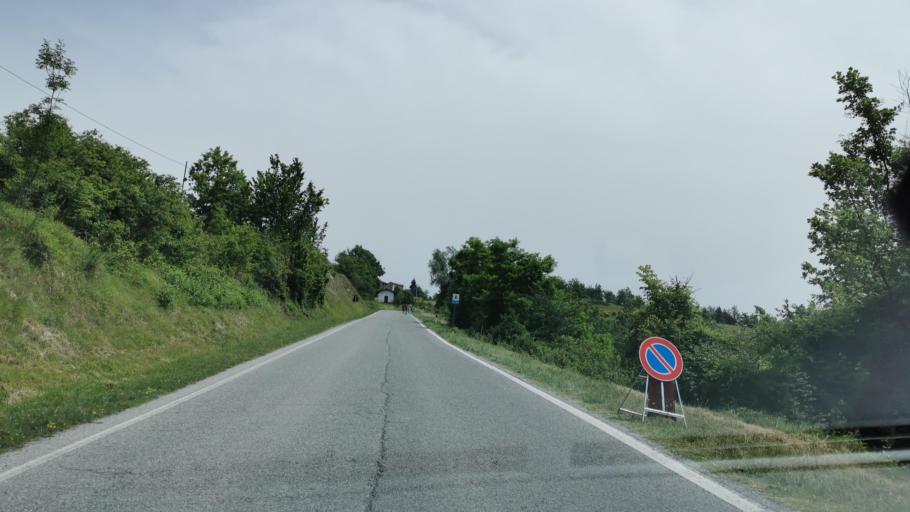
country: IT
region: Piedmont
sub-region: Provincia di Cuneo
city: Sale San Giovanni
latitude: 44.4115
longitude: 8.0788
